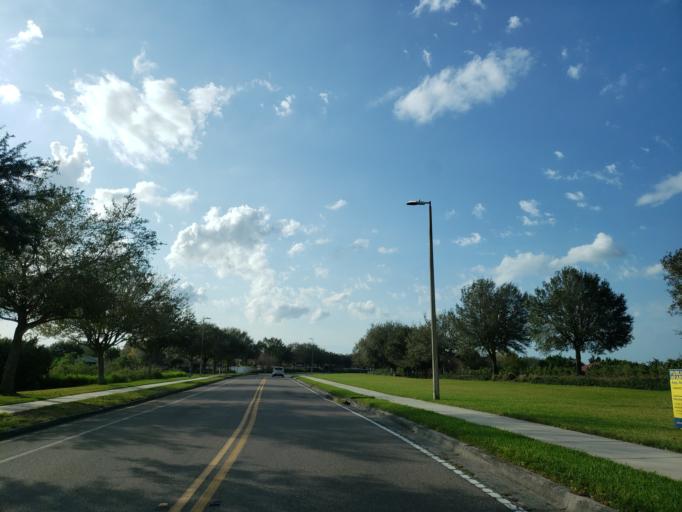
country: US
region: Florida
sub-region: Hillsborough County
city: Riverview
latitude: 27.8330
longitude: -82.3124
